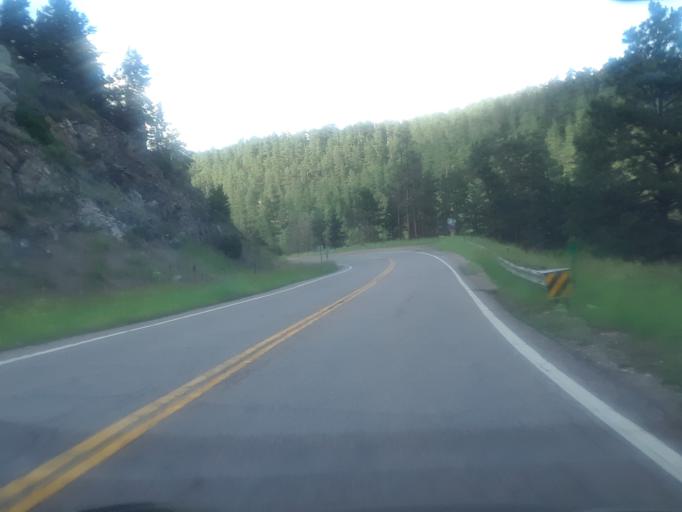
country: US
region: Colorado
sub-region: Jefferson County
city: Kittredge
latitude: 39.7141
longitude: -105.3516
